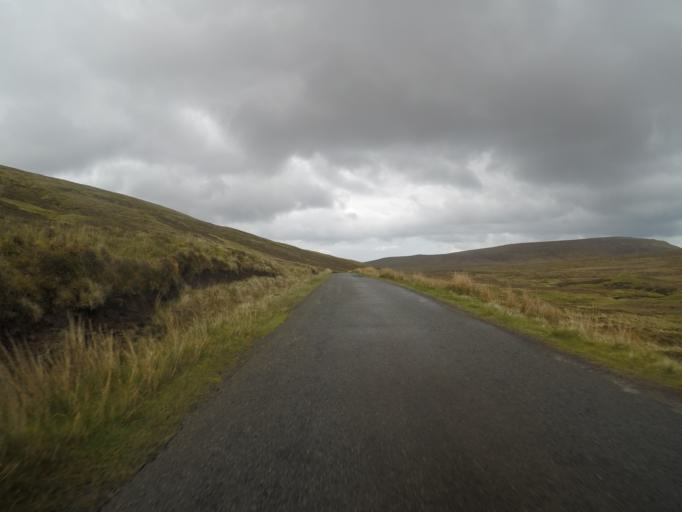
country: GB
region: Scotland
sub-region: Highland
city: Portree
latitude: 57.6226
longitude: -6.3132
